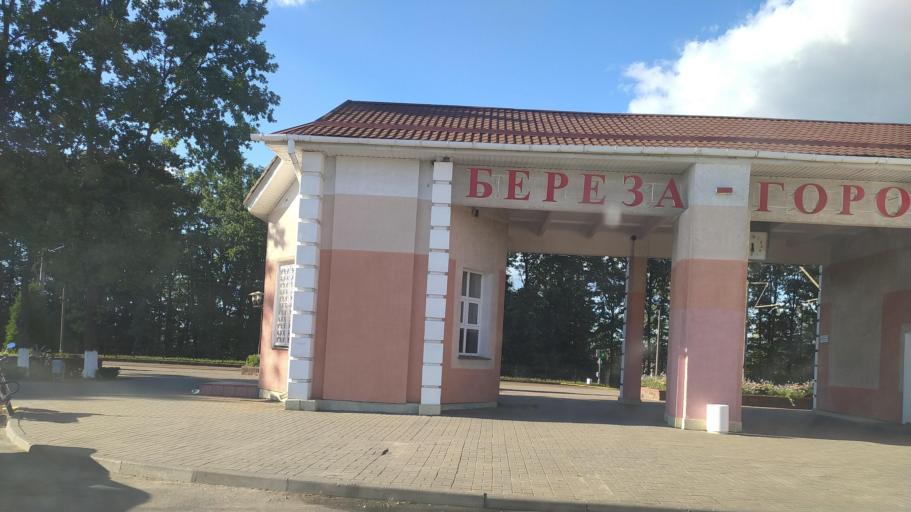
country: BY
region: Brest
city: Byaroza
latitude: 52.5474
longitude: 24.9737
